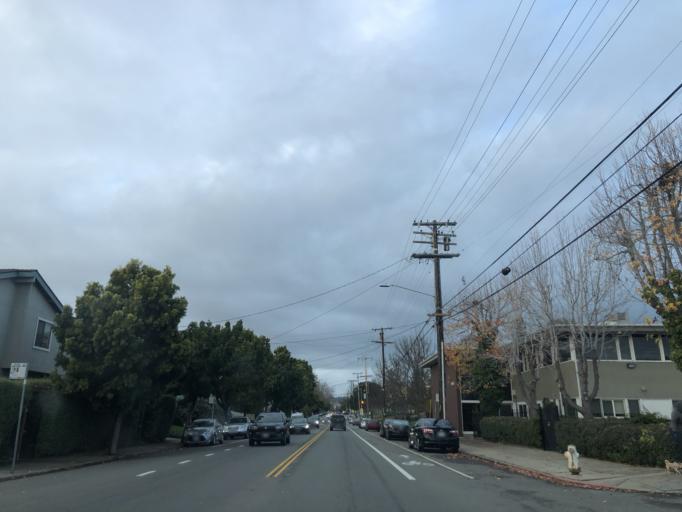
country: US
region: California
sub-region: Alameda County
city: Emeryville
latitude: 37.8445
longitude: -122.2651
